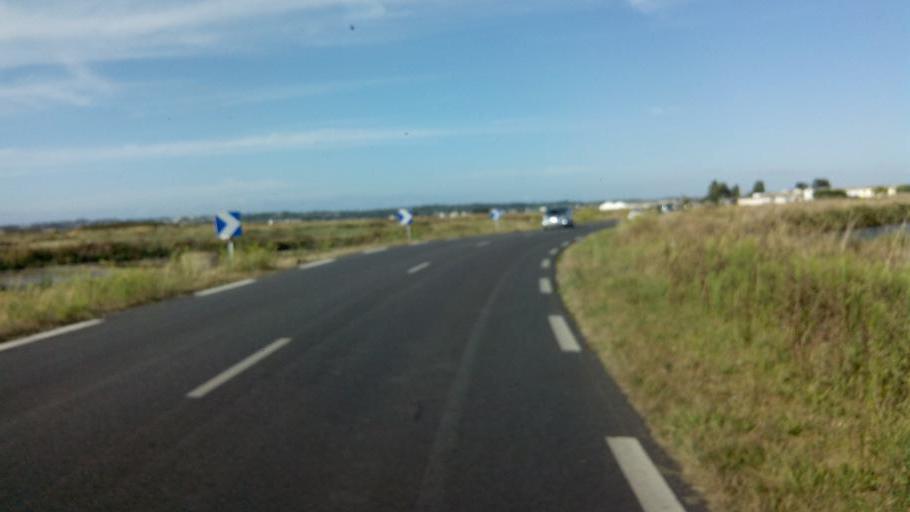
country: FR
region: Pays de la Loire
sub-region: Departement de la Loire-Atlantique
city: Le Pouliguen
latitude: 47.2861
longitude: -2.4492
